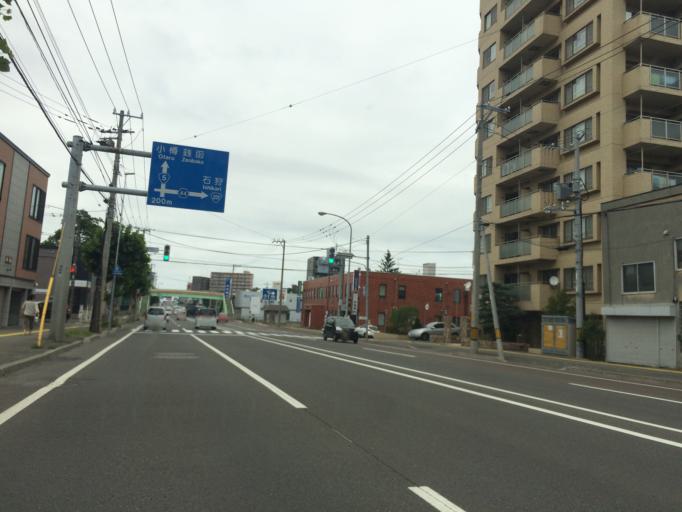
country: JP
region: Hokkaido
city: Sapporo
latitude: 43.1154
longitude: 141.2438
